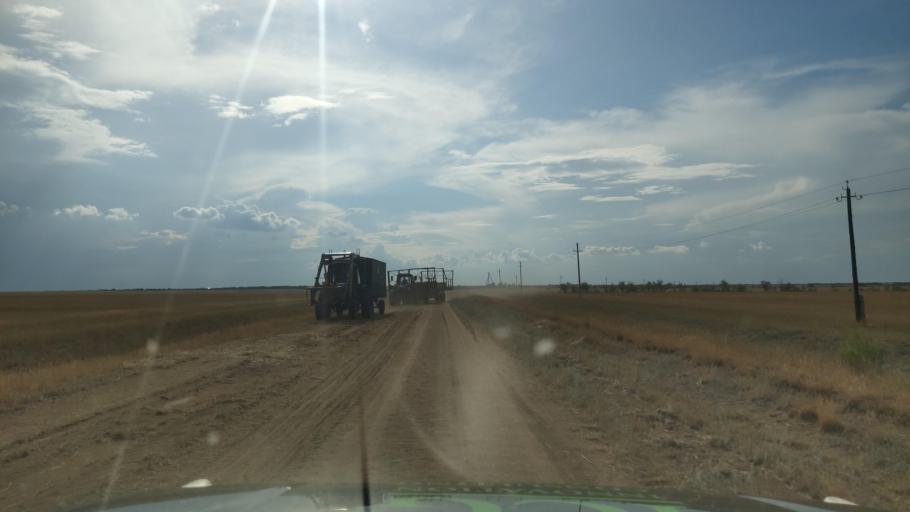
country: KZ
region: Pavlodar
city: Pavlodar
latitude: 52.5130
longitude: 77.4704
